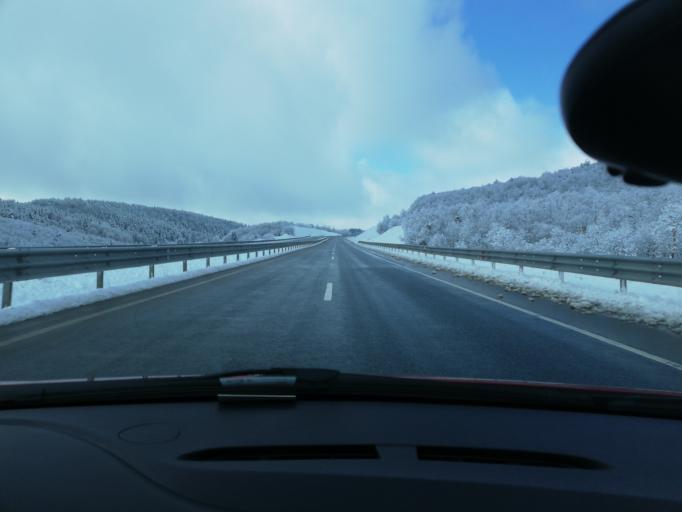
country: TR
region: Kastamonu
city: Ihsangazi
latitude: 41.3284
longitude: 33.6169
